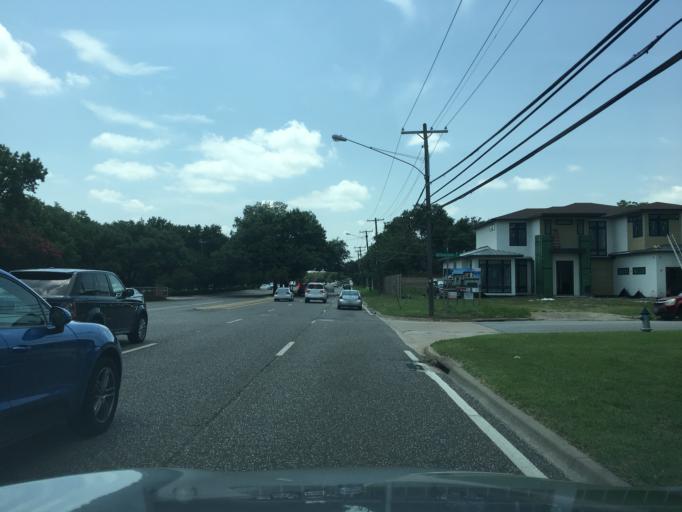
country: US
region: Texas
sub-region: Dallas County
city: Addison
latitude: 32.9155
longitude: -96.8037
